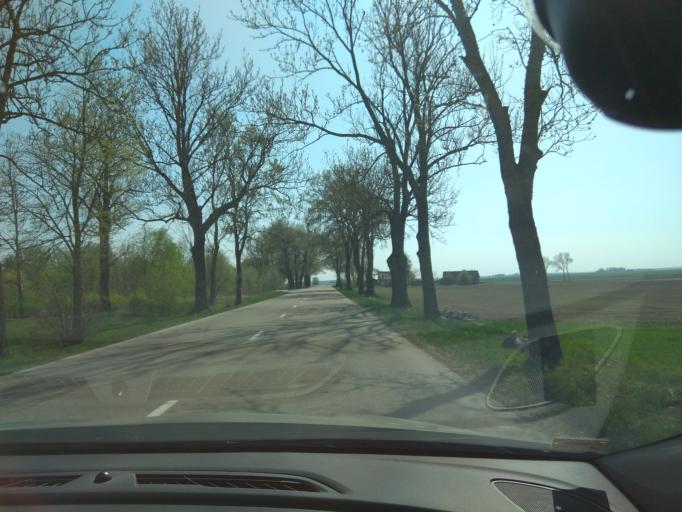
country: LT
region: Panevezys
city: Pasvalys
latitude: 55.9468
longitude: 24.2130
